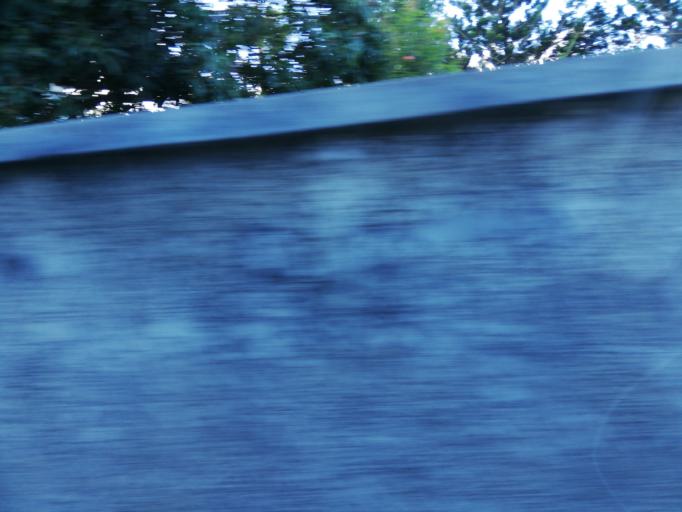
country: MU
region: Moka
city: Moka
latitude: -20.2229
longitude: 57.4749
